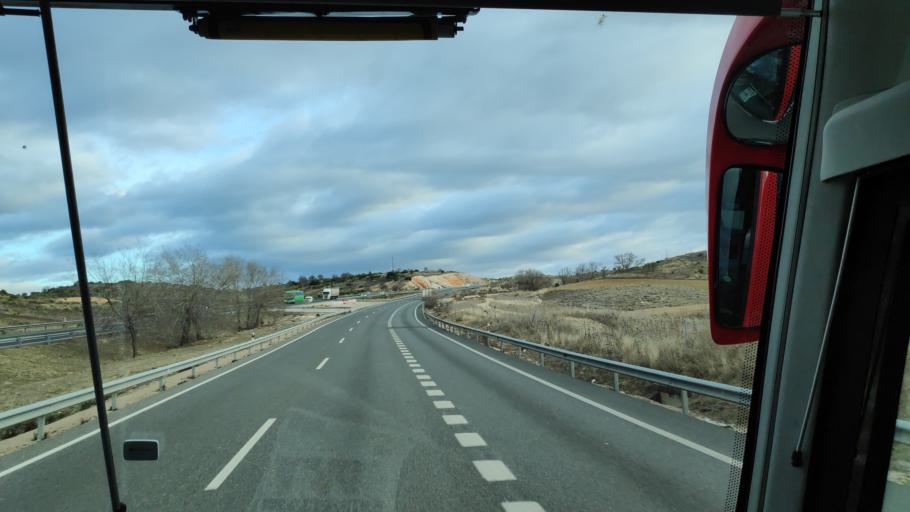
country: ES
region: Madrid
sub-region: Provincia de Madrid
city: Villarejo de Salvanes
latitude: 40.1950
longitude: -3.3042
